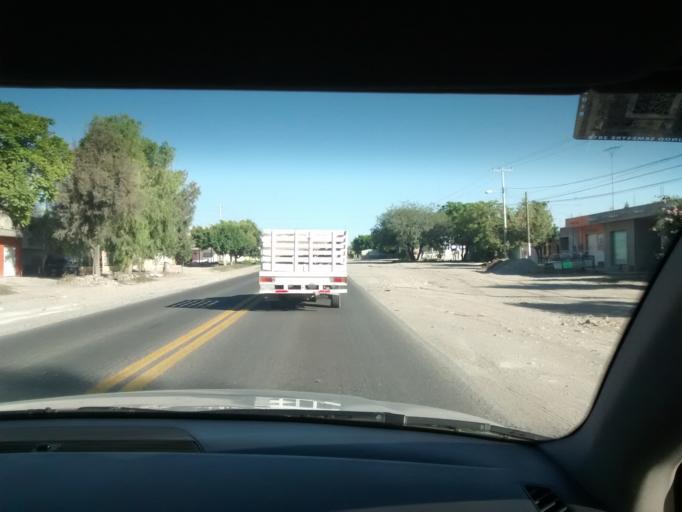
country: MX
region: Puebla
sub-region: Tehuacan
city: Magdalena Cuayucatepec
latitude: 18.5109
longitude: -97.4921
